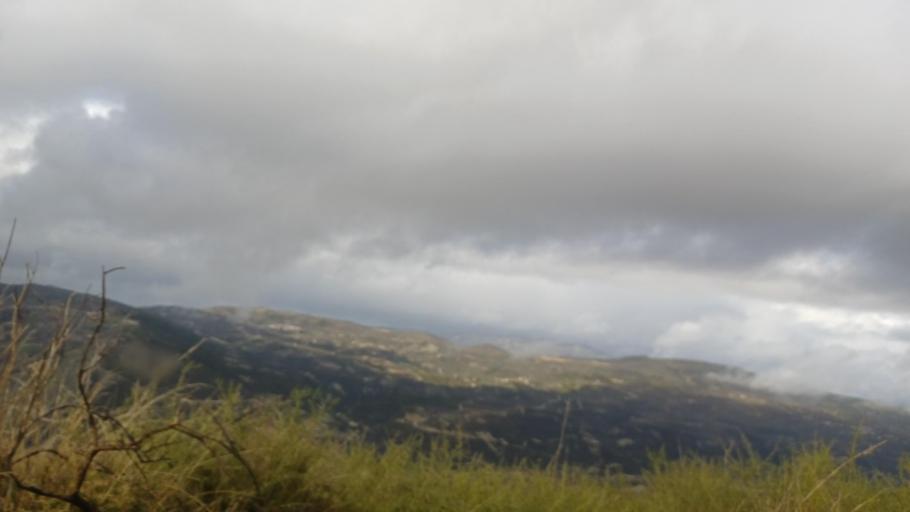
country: CY
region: Limassol
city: Pachna
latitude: 34.8267
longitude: 32.7396
